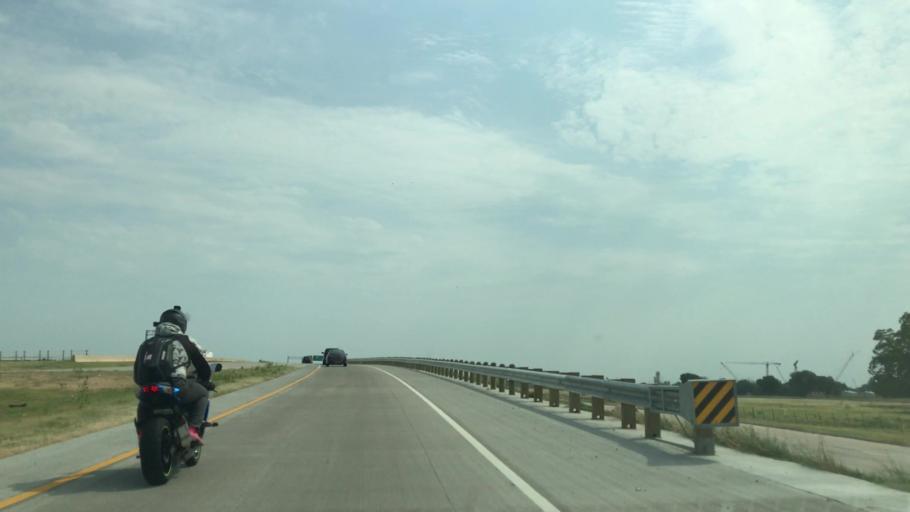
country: US
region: Texas
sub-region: Denton County
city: Roanoke
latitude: 32.9887
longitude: -97.2257
